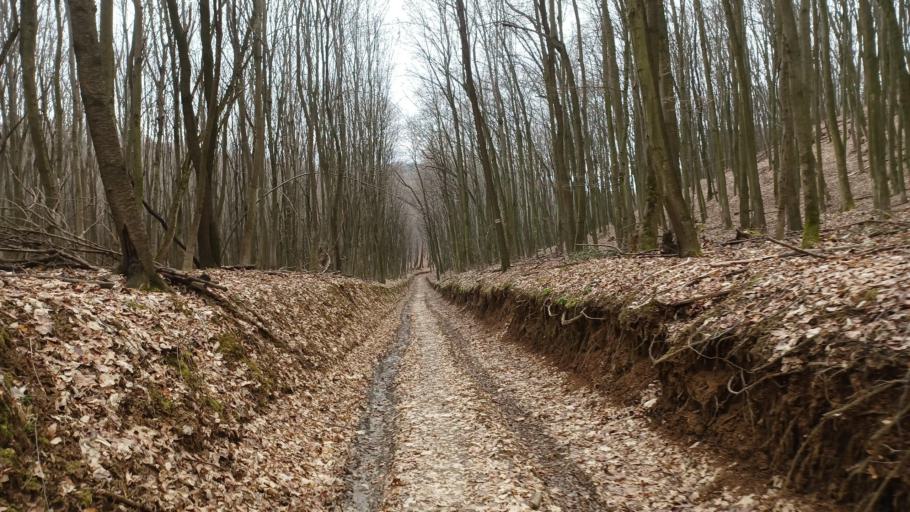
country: HU
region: Tolna
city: Szentgalpuszta
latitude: 46.3257
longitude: 18.6478
